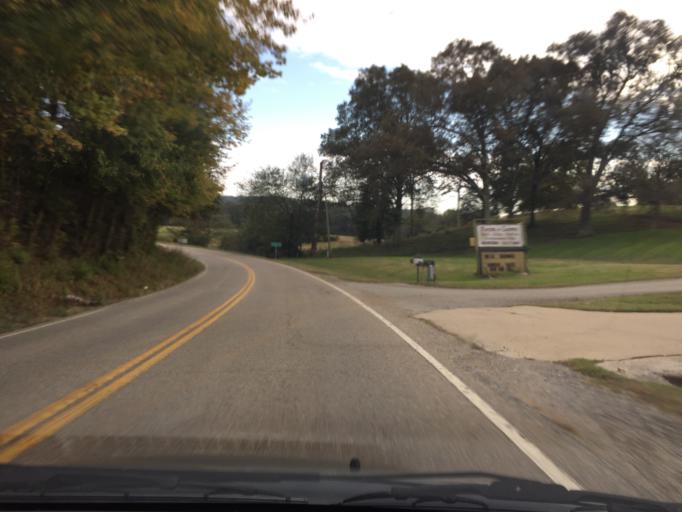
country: US
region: Tennessee
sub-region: Monroe County
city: Sweetwater
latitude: 35.6303
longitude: -84.5047
